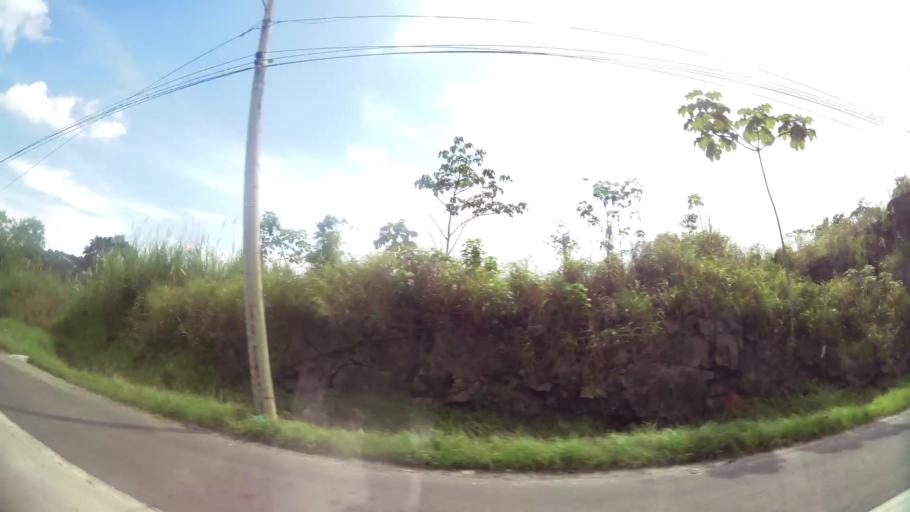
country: PA
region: Panama
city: Las Cumbres
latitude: 9.0401
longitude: -79.5545
